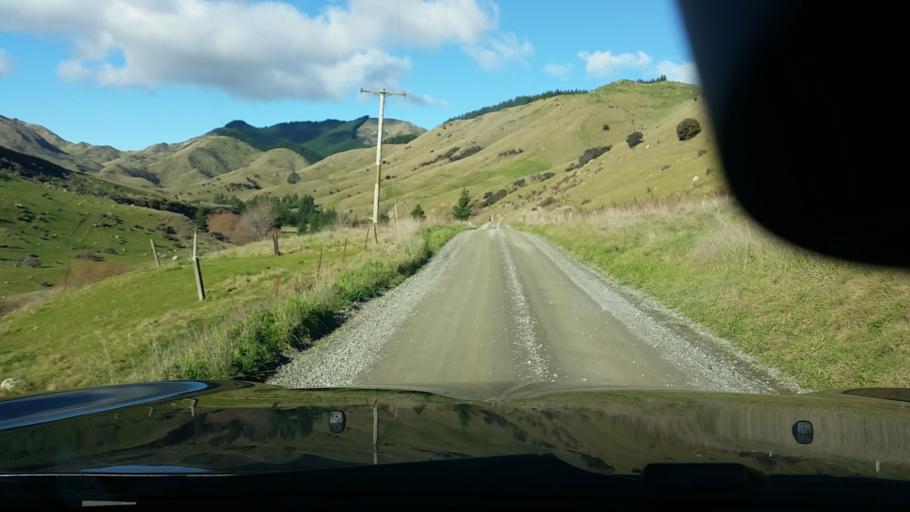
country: NZ
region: Marlborough
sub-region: Marlborough District
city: Blenheim
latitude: -41.6012
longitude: 173.9543
